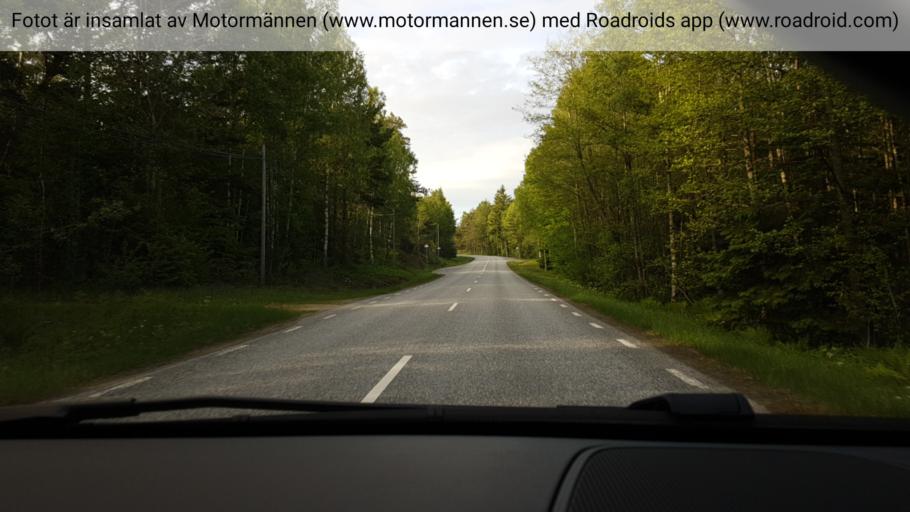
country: SE
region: Stockholm
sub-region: Haninge Kommun
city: Jordbro
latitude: 58.9891
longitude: 18.0976
